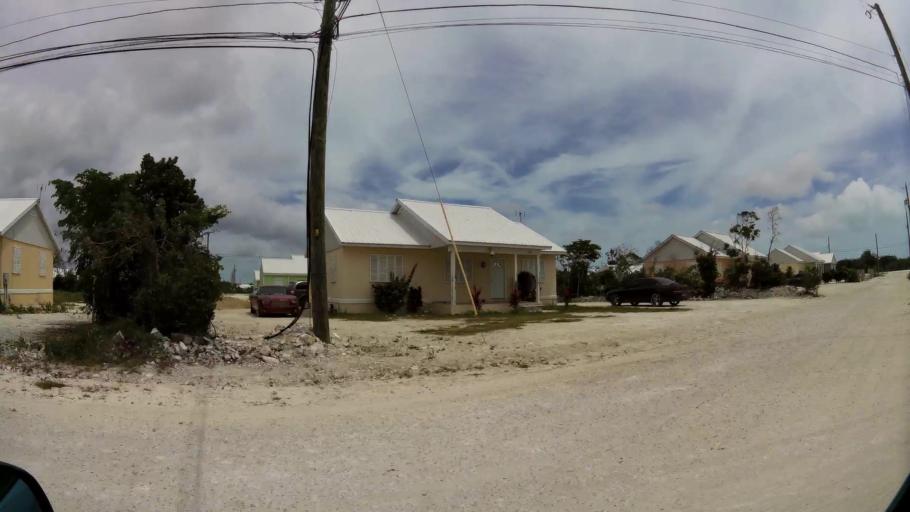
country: BS
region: Mayaguana
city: Abraham's Bay
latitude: 21.8059
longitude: -72.2961
